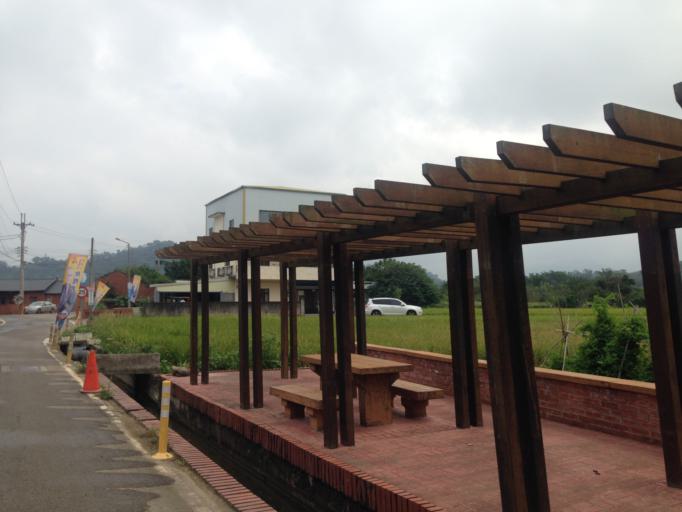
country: TW
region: Taiwan
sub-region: Hsinchu
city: Hsinchu
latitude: 24.6764
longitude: 120.9543
